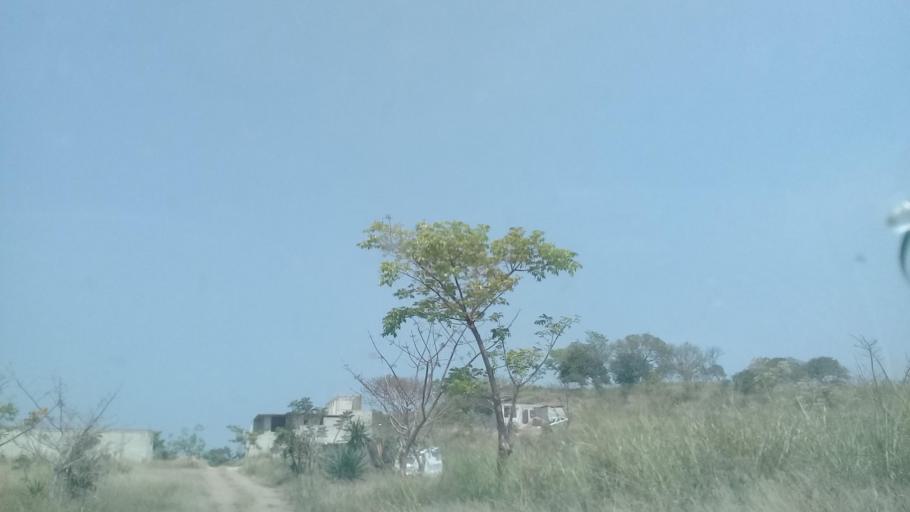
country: MX
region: Veracruz
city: El Castillo
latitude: 19.5642
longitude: -96.8417
